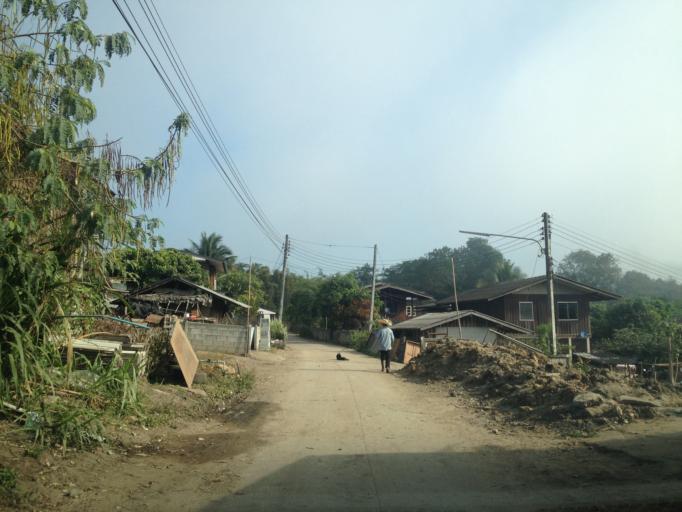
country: TH
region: Mae Hong Son
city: Ban Huai I Huak
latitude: 18.0964
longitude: 98.2069
